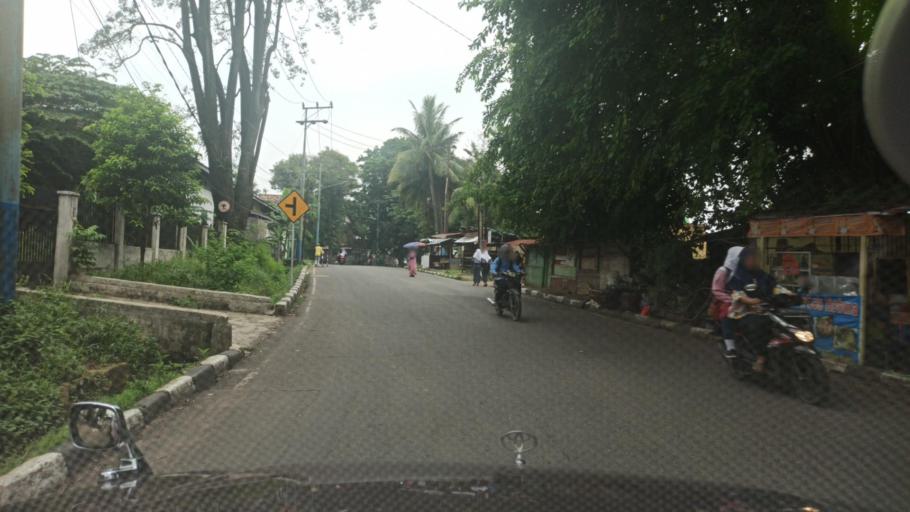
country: ID
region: South Sumatra
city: Plaju
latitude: -2.9955
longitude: 104.7473
